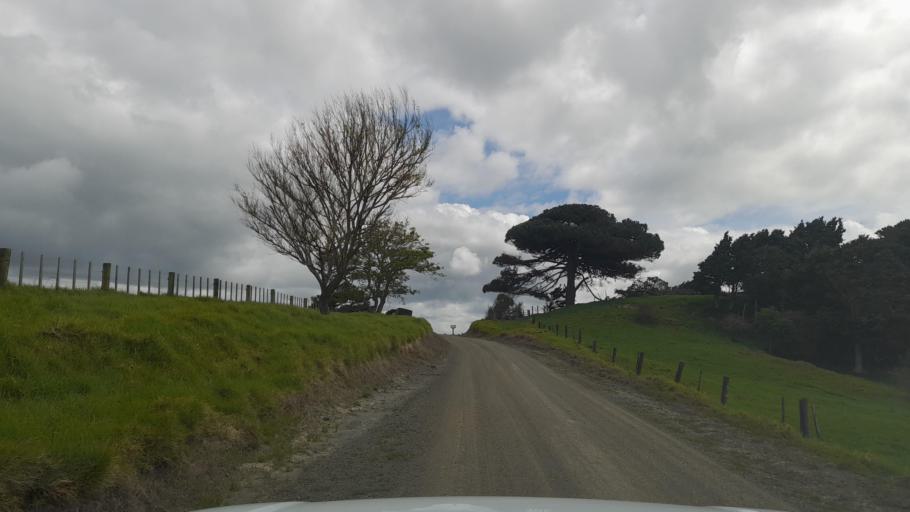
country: NZ
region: Auckland
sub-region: Auckland
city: Wellsford
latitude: -36.2173
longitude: 174.3208
